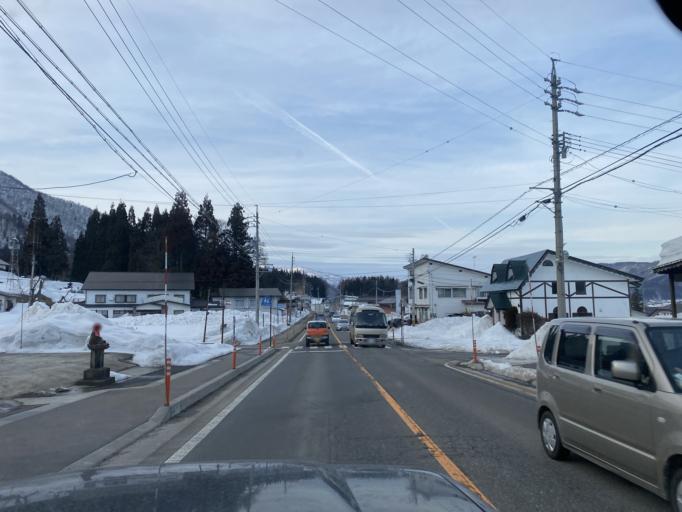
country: JP
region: Nagano
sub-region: Kitaazumi Gun
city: Hakuba
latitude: 36.6327
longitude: 137.8447
